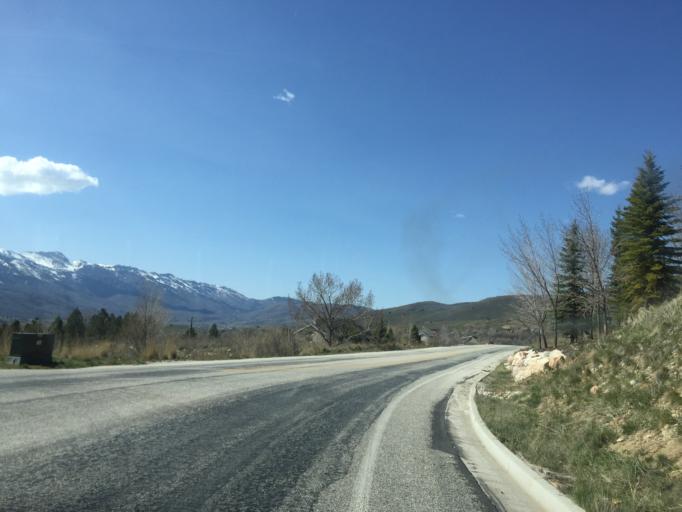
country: US
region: Utah
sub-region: Weber County
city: Wolf Creek
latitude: 41.3304
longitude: -111.8250
